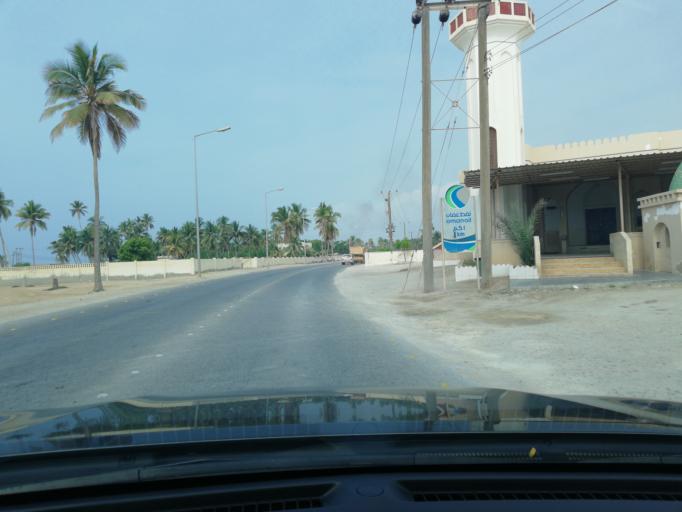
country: OM
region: Zufar
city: Salalah
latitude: 17.0049
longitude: 54.1235
